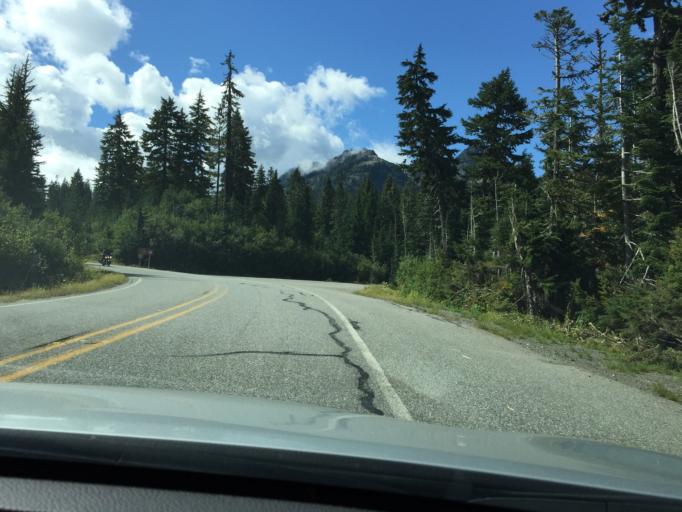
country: CA
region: British Columbia
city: Agassiz
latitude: 48.8660
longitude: -121.6657
